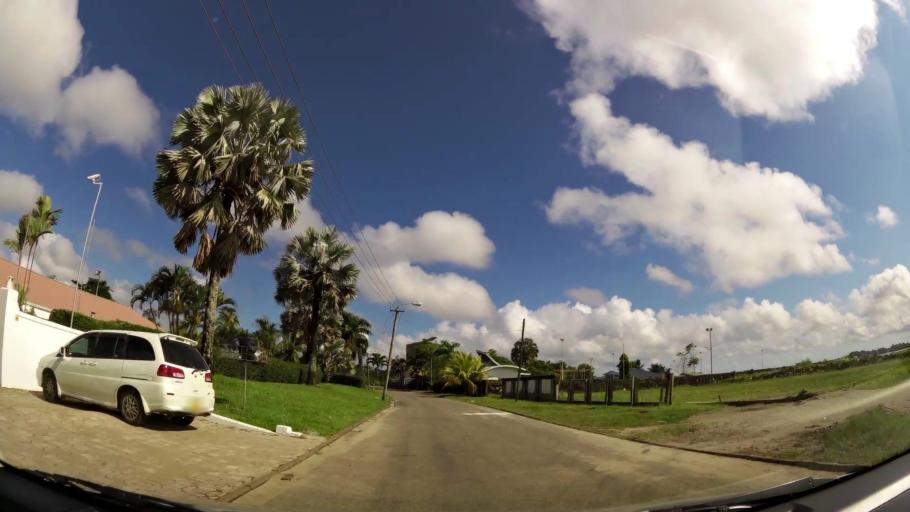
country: SR
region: Commewijne
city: Nieuw Amsterdam
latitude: 5.8716
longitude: -55.1003
